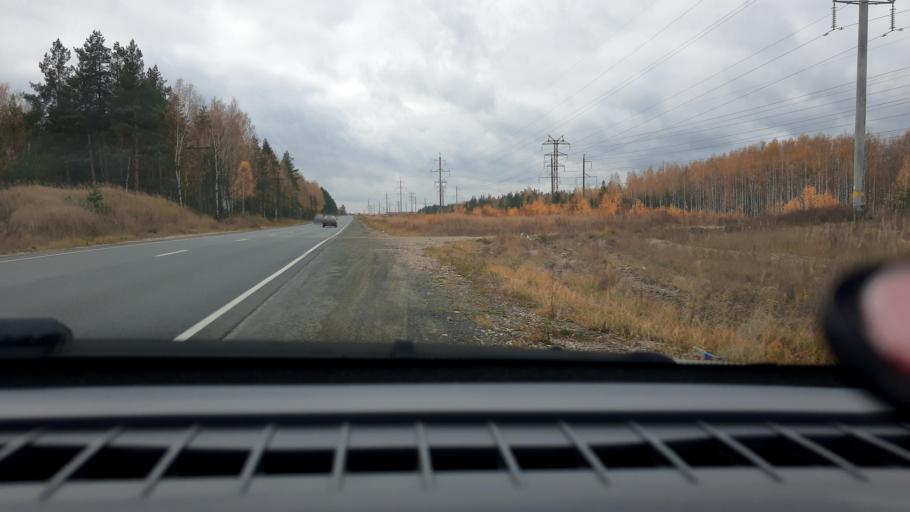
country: RU
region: Nizjnij Novgorod
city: Lukino
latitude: 56.3517
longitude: 43.5884
